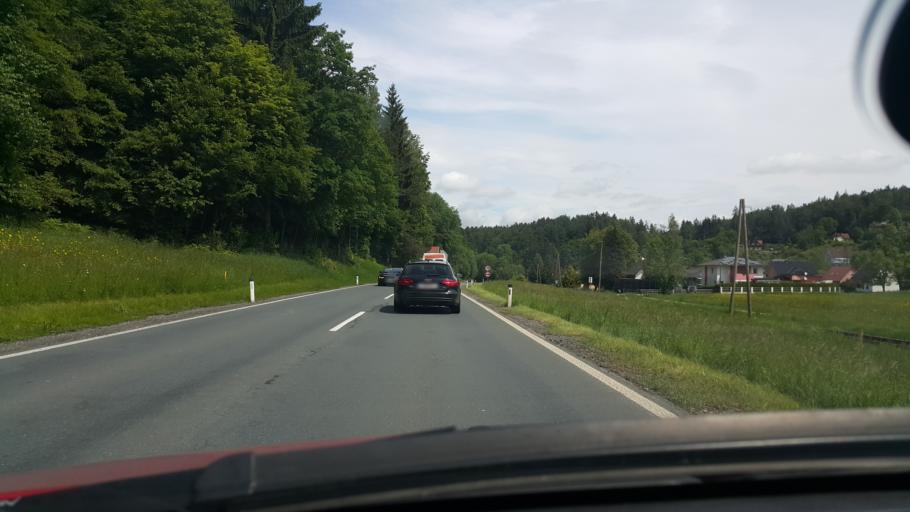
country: AT
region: Carinthia
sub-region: Politischer Bezirk Klagenfurt Land
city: Maria Rain
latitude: 46.5703
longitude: 14.2856
